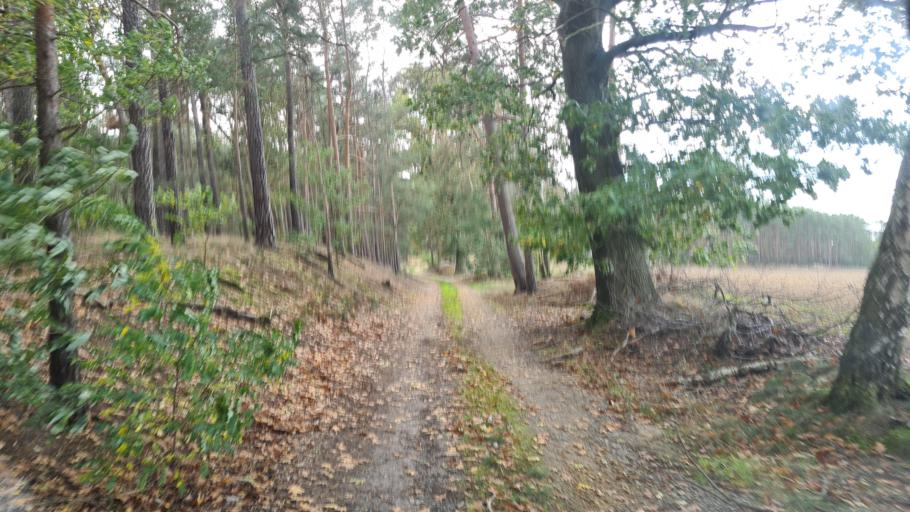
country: DE
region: Brandenburg
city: Bronkow
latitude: 51.7351
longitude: 13.8613
